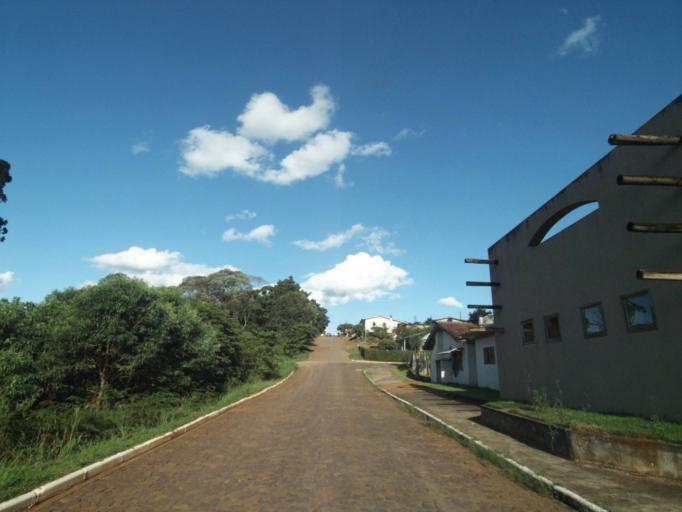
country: BR
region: Parana
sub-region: Uniao Da Vitoria
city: Uniao da Vitoria
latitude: -26.1598
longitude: -51.5391
